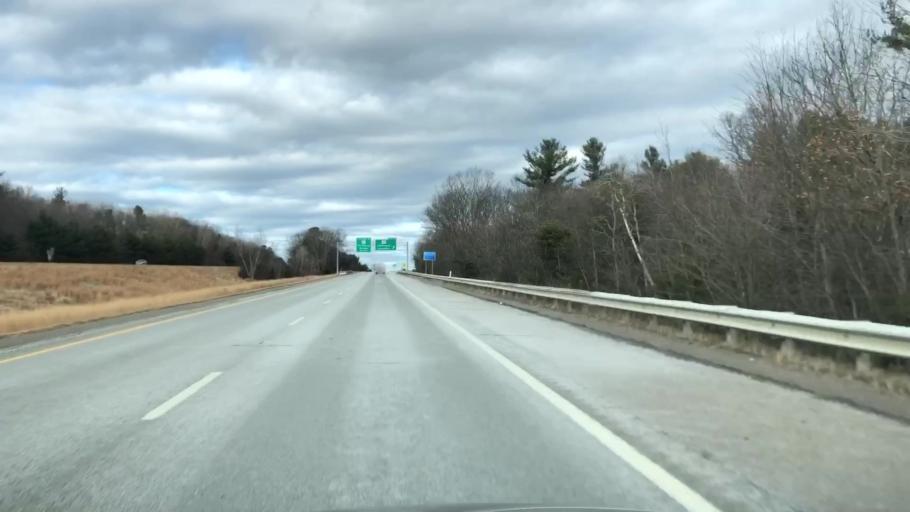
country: US
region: Massachusetts
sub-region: Worcester County
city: South Lancaster
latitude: 42.4827
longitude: -71.7229
